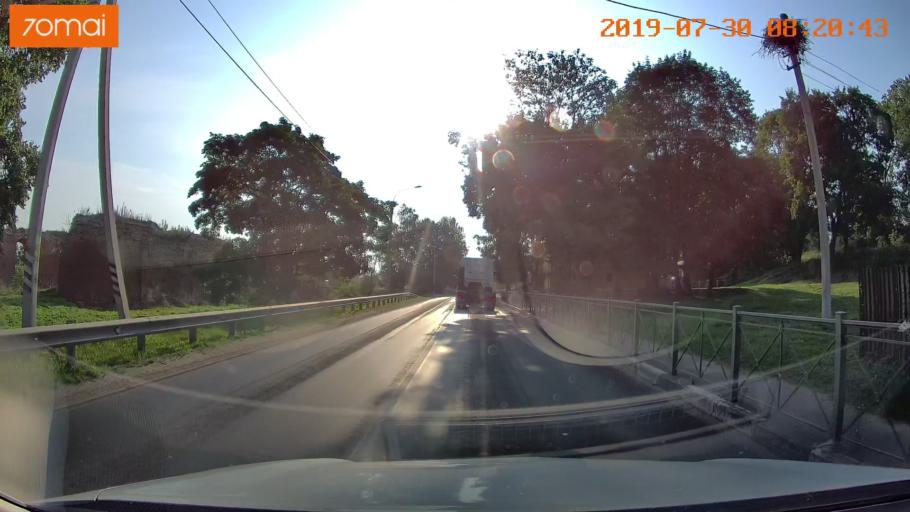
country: RU
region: Kaliningrad
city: Chernyakhovsk
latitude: 54.6263
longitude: 21.5205
